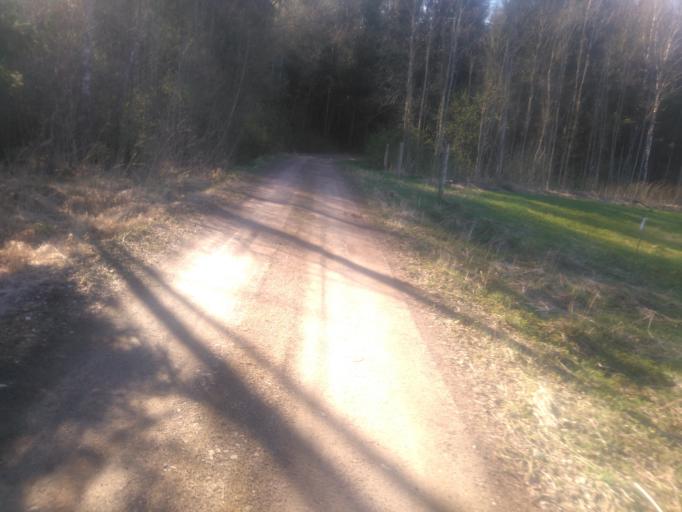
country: LV
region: Vecpiebalga
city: Vecpiebalga
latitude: 57.0072
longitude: 25.8451
